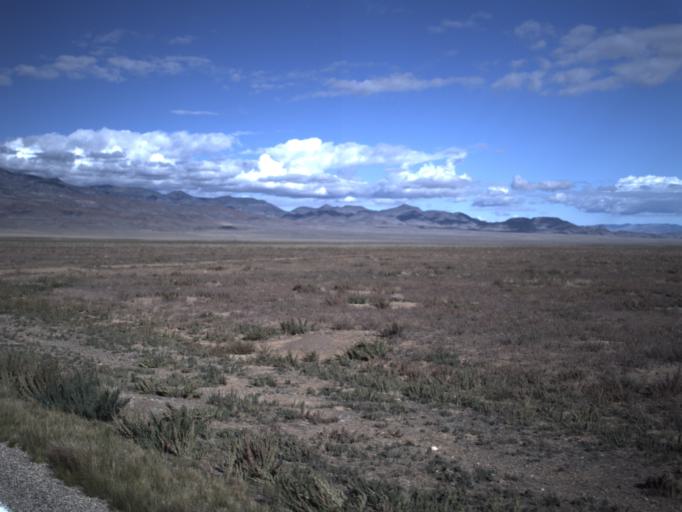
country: US
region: Utah
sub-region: Beaver County
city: Milford
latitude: 38.4614
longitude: -113.3791
